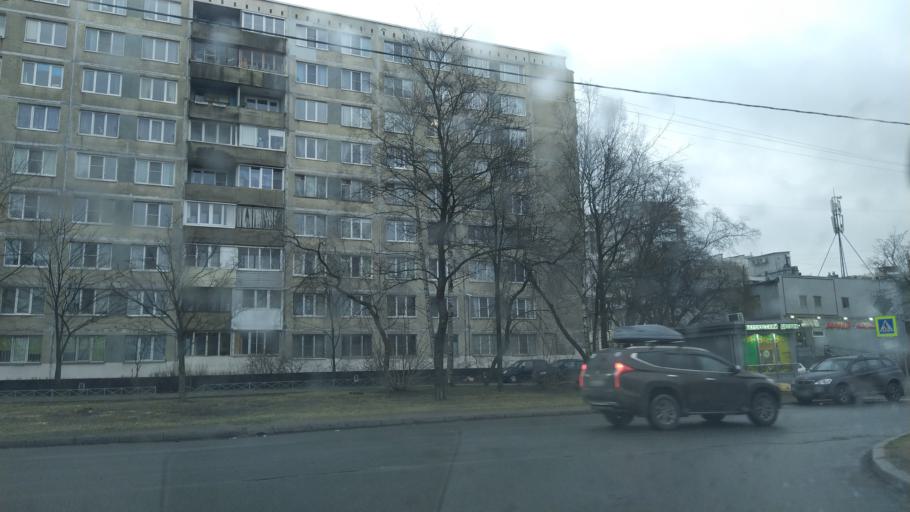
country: RU
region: Leningrad
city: Akademicheskoe
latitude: 60.0228
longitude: 30.3926
